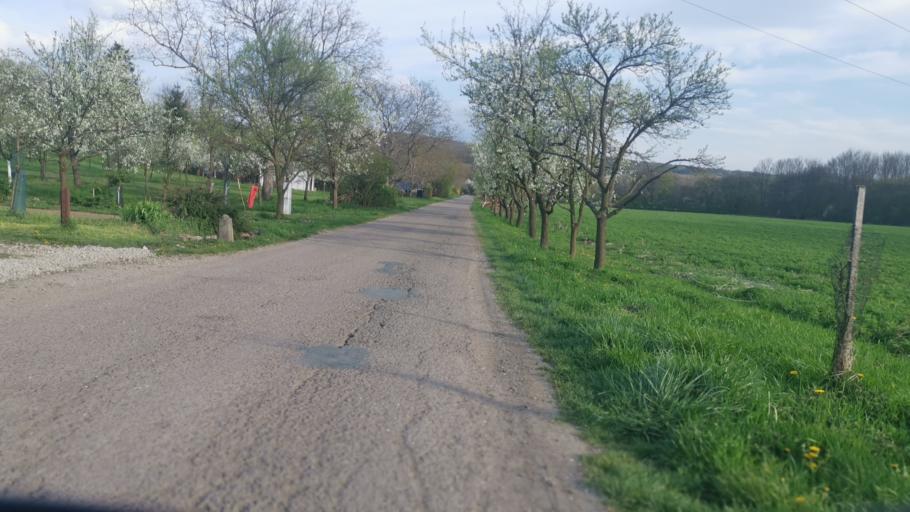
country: CZ
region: South Moravian
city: Petrov
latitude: 48.8477
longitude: 17.3020
